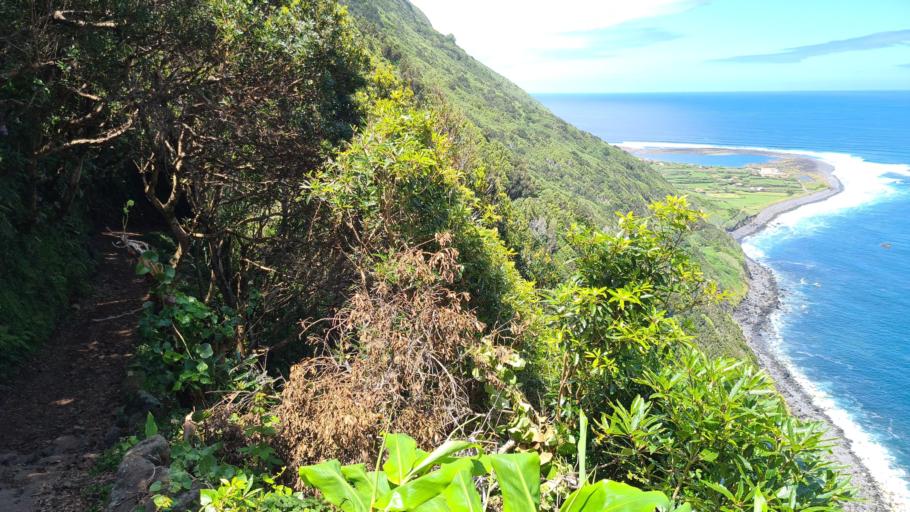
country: PT
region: Azores
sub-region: Sao Roque do Pico
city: Sao Roque do Pico
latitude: 38.6167
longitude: -27.9203
